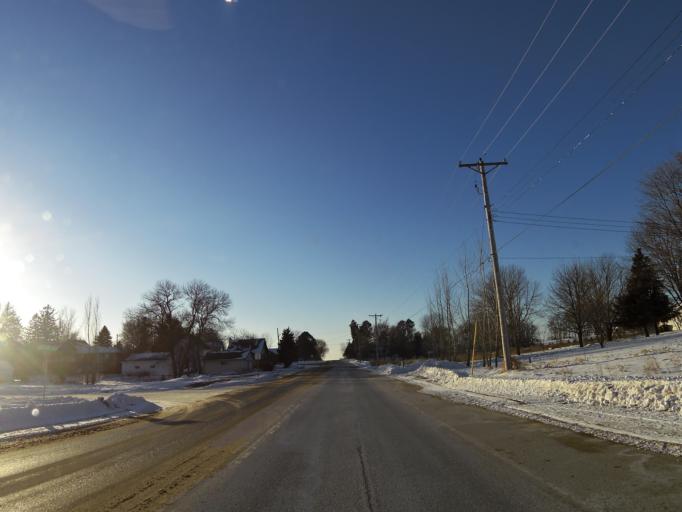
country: US
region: Minnesota
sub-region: Rice County
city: Lonsdale
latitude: 44.4864
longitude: -93.4266
